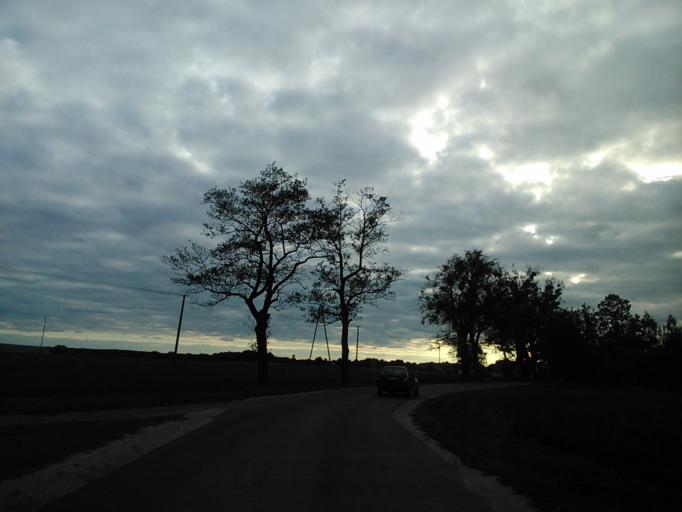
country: PL
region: Kujawsko-Pomorskie
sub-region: Powiat golubsko-dobrzynski
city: Kowalewo Pomorskie
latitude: 53.1282
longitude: 18.9395
